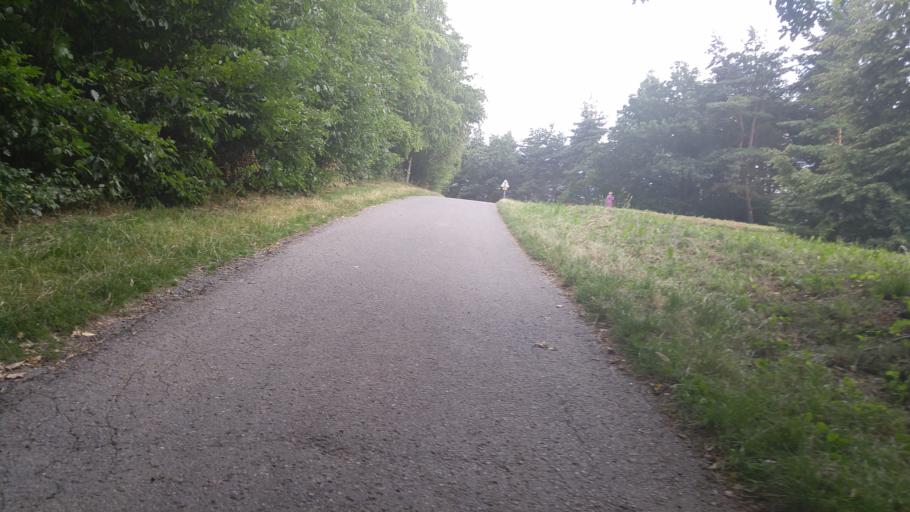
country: CZ
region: Central Bohemia
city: Horomerice
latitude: 50.1003
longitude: 14.3374
